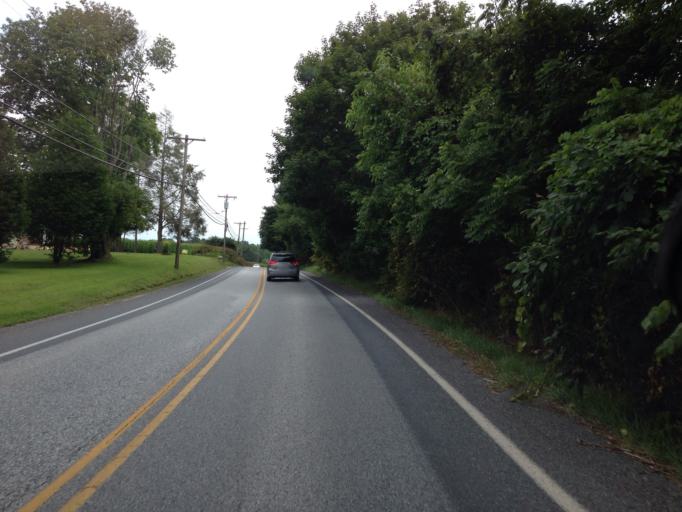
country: US
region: Delaware
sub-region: New Castle County
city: Newark
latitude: 39.7384
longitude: -75.7979
